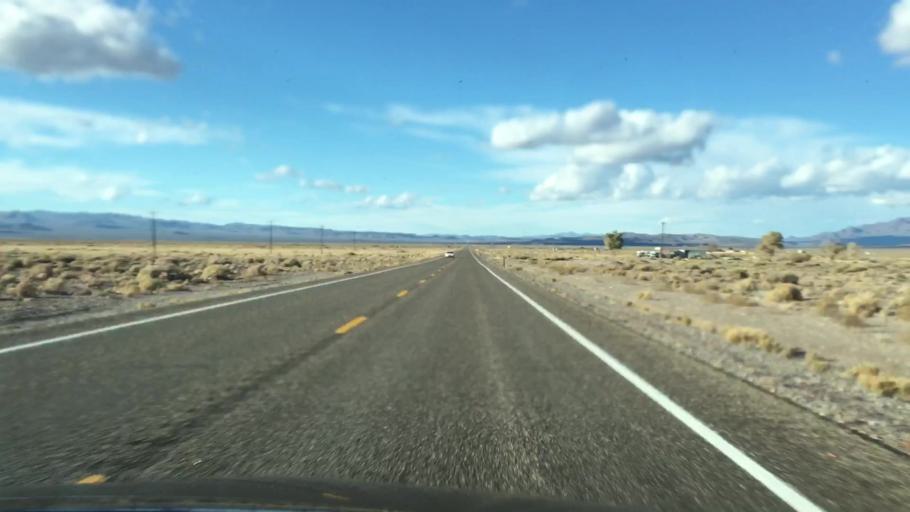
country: US
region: Nevada
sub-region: Nye County
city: Beatty
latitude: 37.2483
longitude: -117.0020
